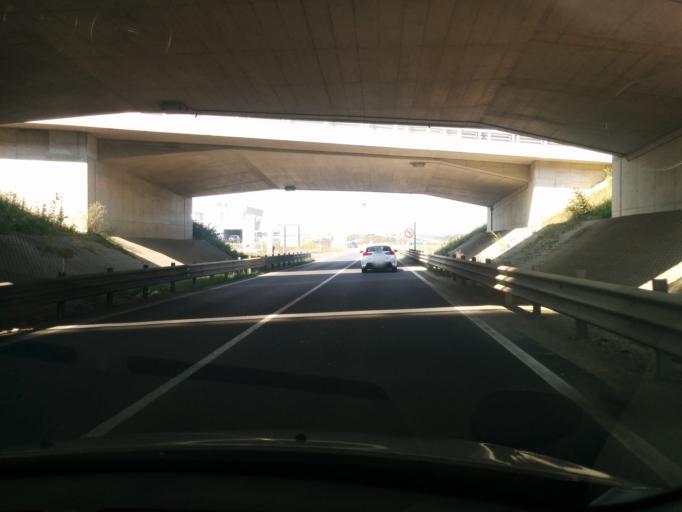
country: AT
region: Lower Austria
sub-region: Politischer Bezirk Mistelbach
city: Grossebersdorf
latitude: 48.3470
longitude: 16.4739
